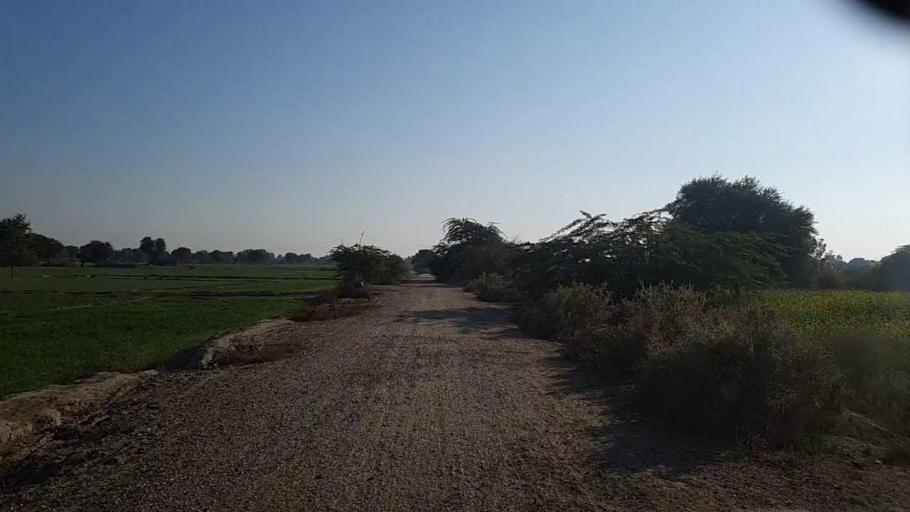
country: PK
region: Sindh
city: Darya Khan Marri
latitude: 26.6896
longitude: 68.3625
